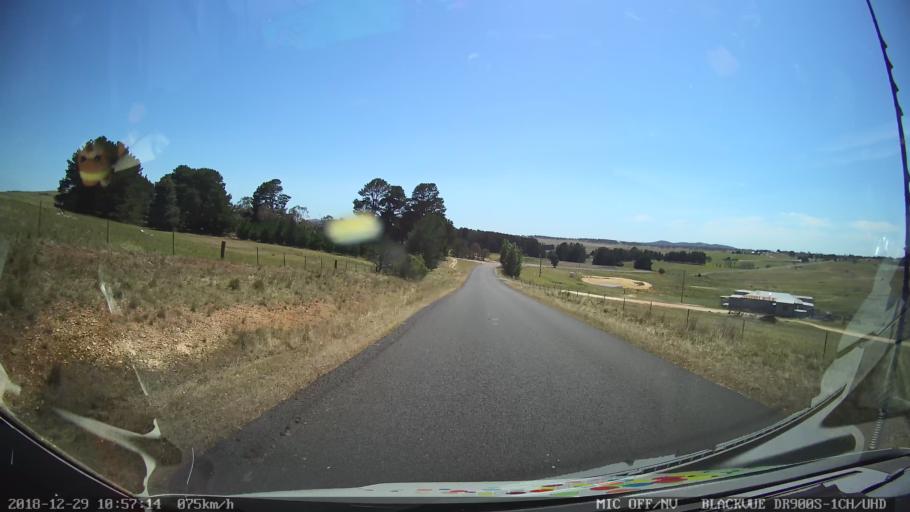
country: AU
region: New South Wales
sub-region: Palerang
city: Bungendore
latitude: -35.1378
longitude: 149.5455
